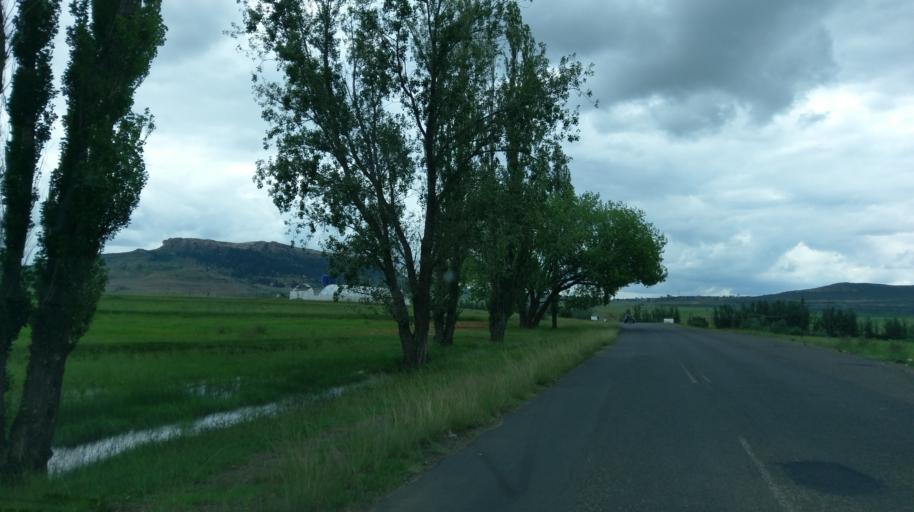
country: LS
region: Berea
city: Teyateyaneng
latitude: -29.0926
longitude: 27.7489
